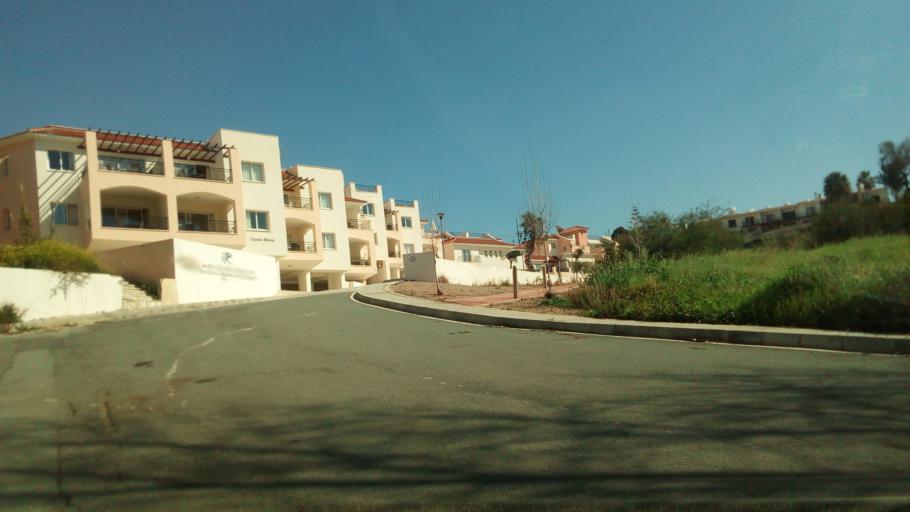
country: CY
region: Pafos
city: Chlorakas
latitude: 34.8058
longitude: 32.4046
